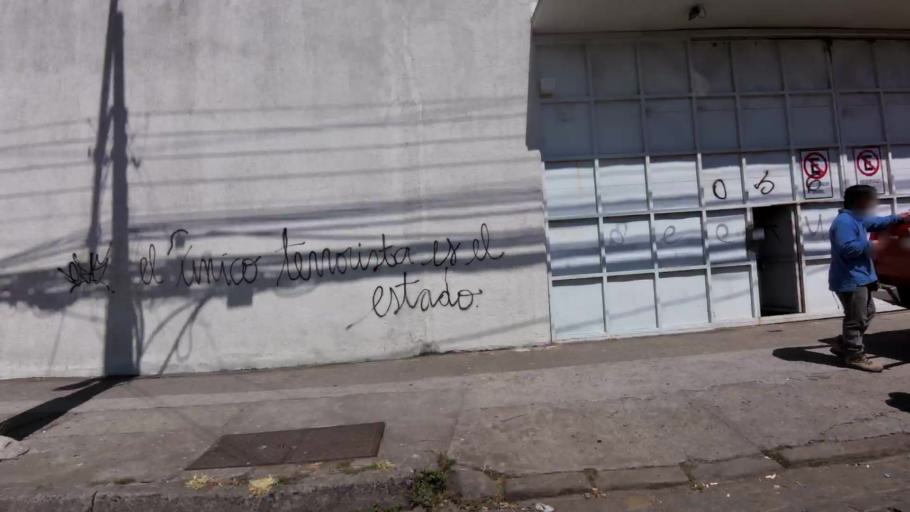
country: CL
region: Biobio
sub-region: Provincia de Concepcion
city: Concepcion
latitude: -36.8211
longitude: -73.0528
